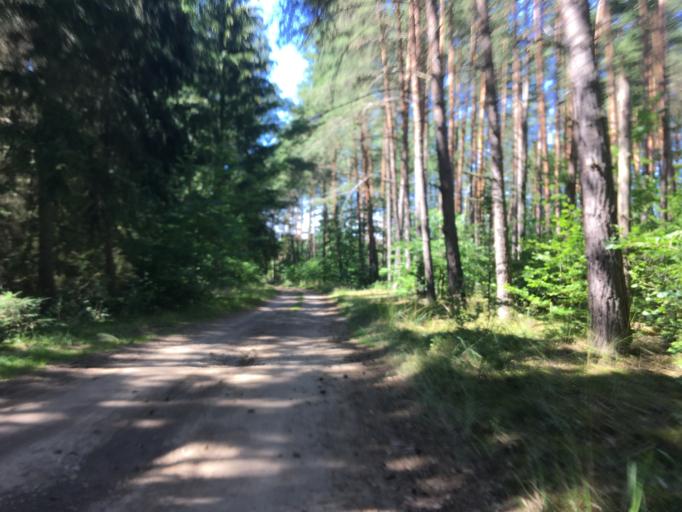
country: DE
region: Brandenburg
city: Rheinsberg
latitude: 53.1304
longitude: 12.9510
